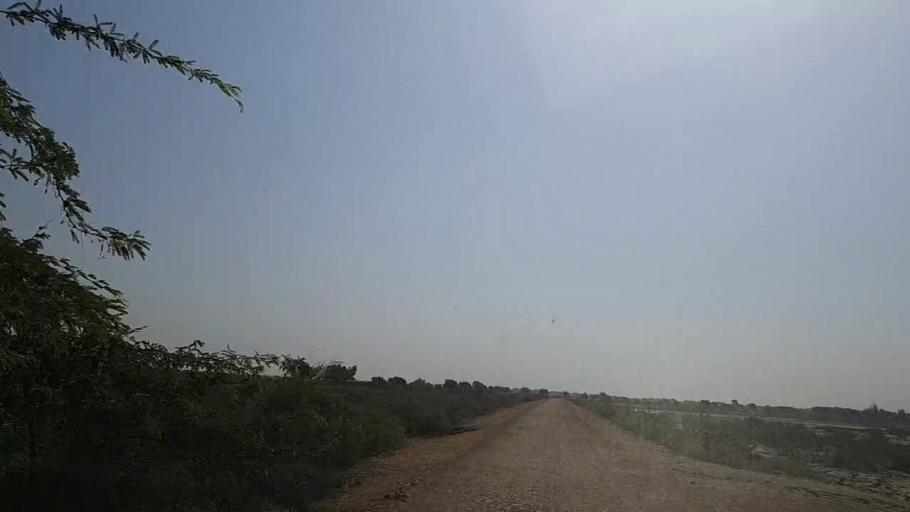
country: PK
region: Sindh
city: Daro Mehar
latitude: 24.7101
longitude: 68.1236
